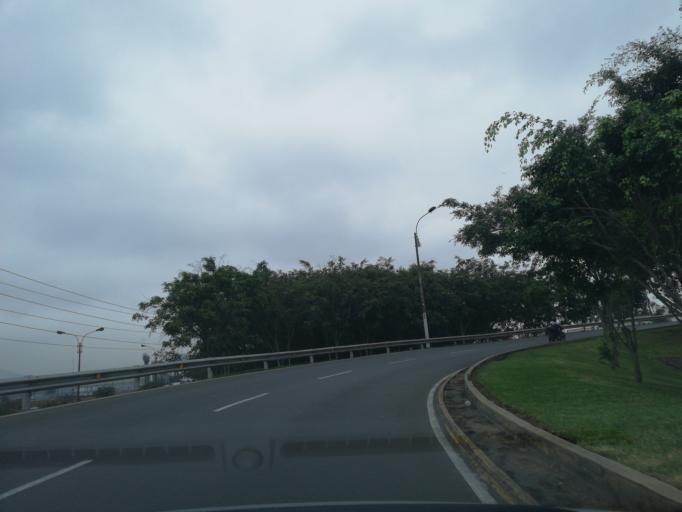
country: PE
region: Lima
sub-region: Lima
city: San Luis
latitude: -12.0856
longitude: -76.9814
